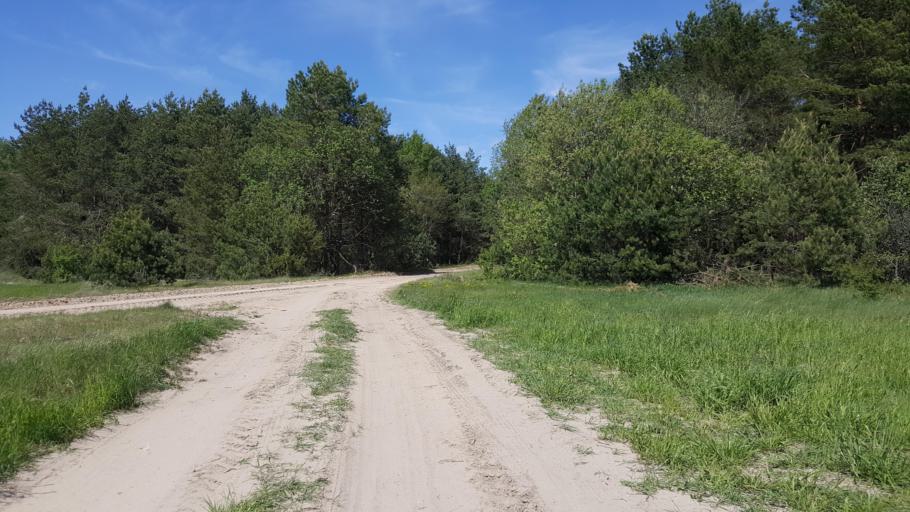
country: BY
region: Brest
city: Zhabinka
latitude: 52.3633
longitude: 24.1583
